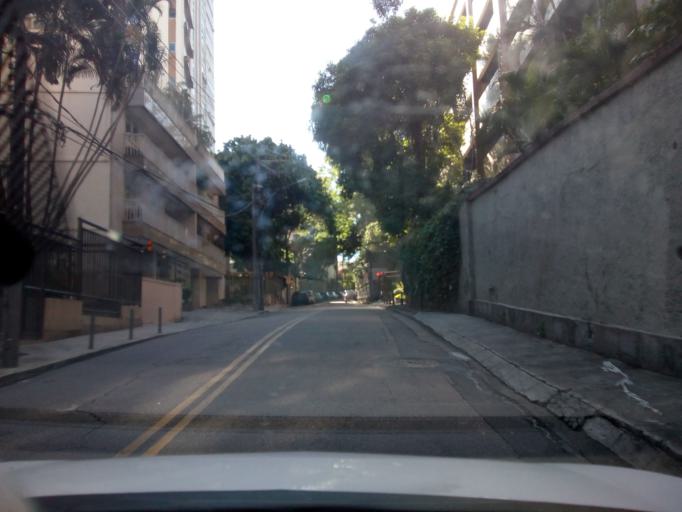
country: BR
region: Rio de Janeiro
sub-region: Rio De Janeiro
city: Rio de Janeiro
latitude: -22.9844
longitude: -43.2330
